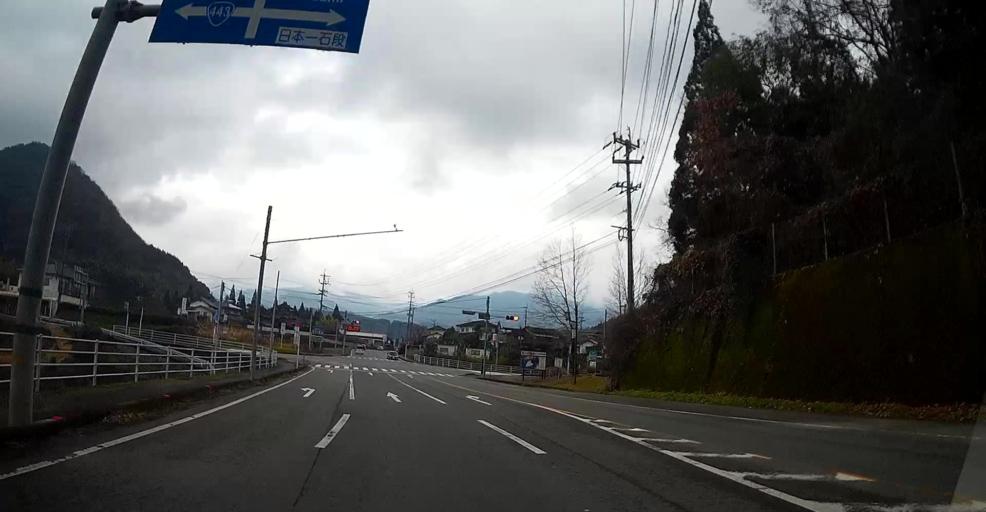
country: JP
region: Kumamoto
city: Matsubase
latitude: 32.6264
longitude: 130.8121
